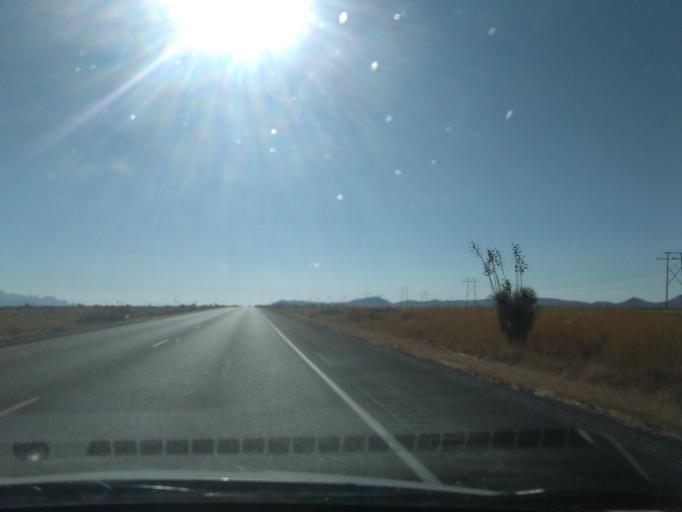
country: US
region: New Mexico
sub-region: Luna County
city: Deming
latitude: 32.4651
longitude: -107.5401
